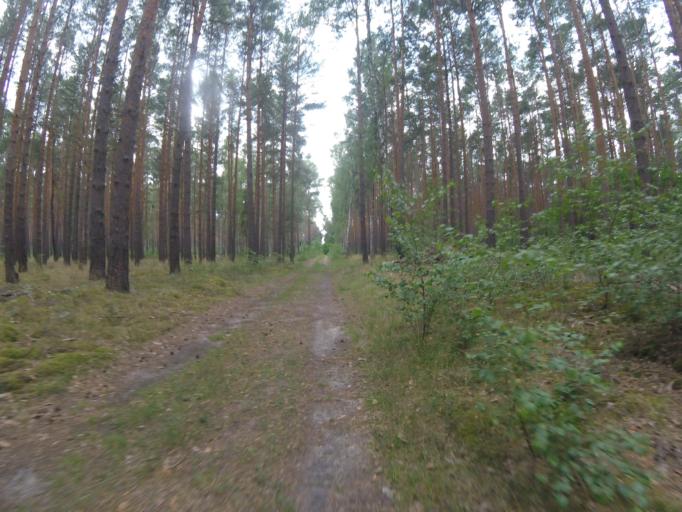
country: DE
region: Brandenburg
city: Schwerin
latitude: 52.1860
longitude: 13.6088
